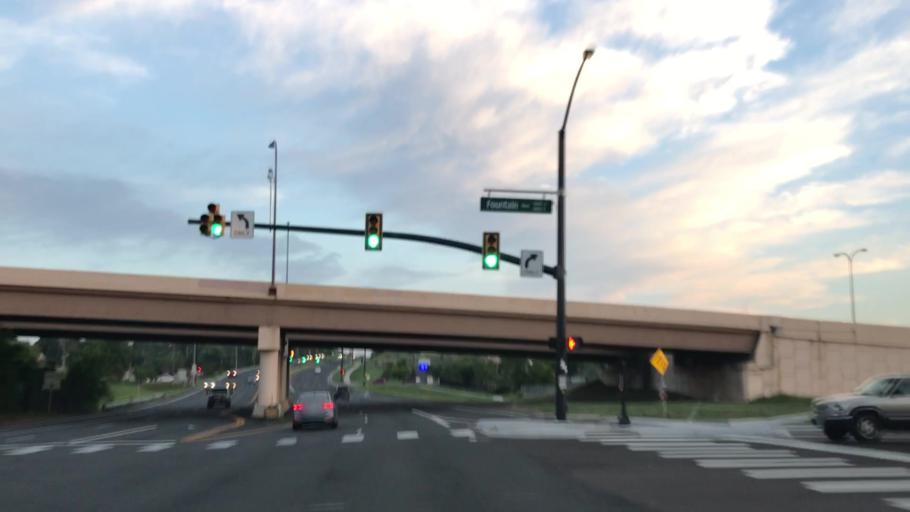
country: US
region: Colorado
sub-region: El Paso County
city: Stratmoor
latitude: 38.8176
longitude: -104.7807
